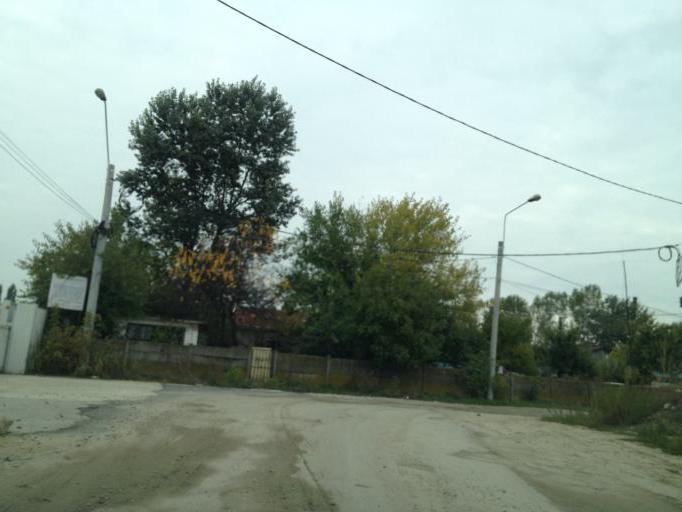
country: RO
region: Dolj
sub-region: Municipiul Craiova
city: Popoveni
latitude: 44.2935
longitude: 23.7934
